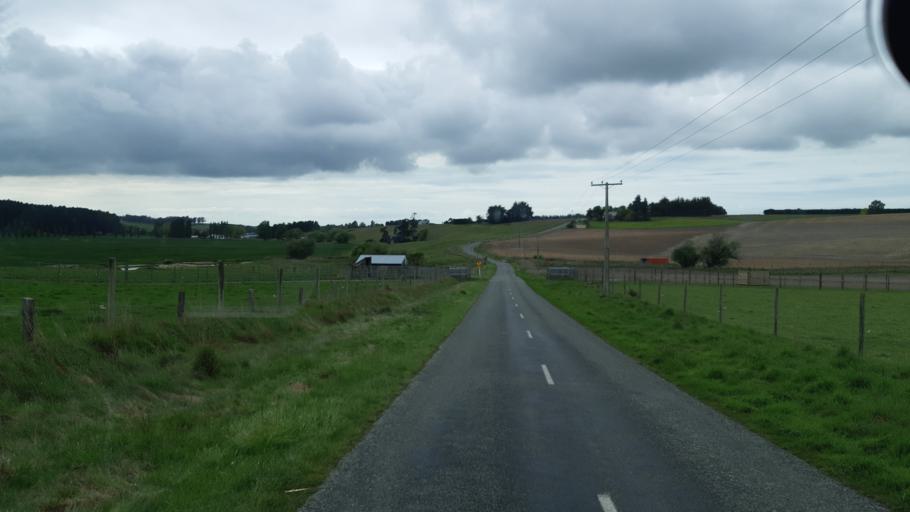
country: NZ
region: Canterbury
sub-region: Timaru District
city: Pleasant Point
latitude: -44.3288
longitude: 171.1493
